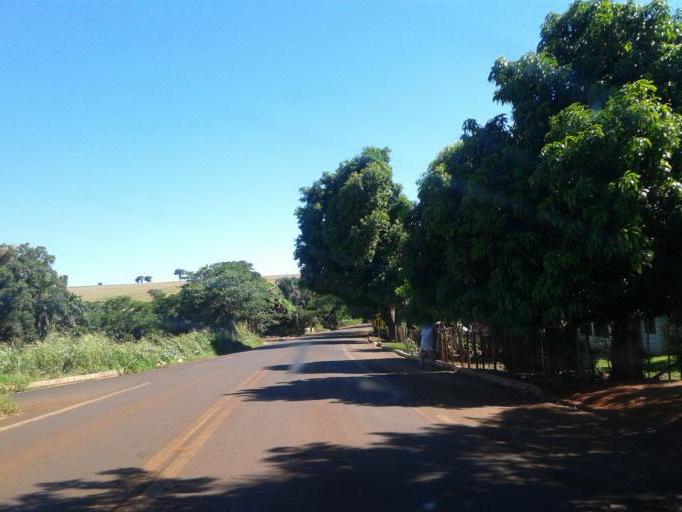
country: BR
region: Minas Gerais
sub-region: Capinopolis
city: Capinopolis
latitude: -18.6782
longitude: -49.5646
